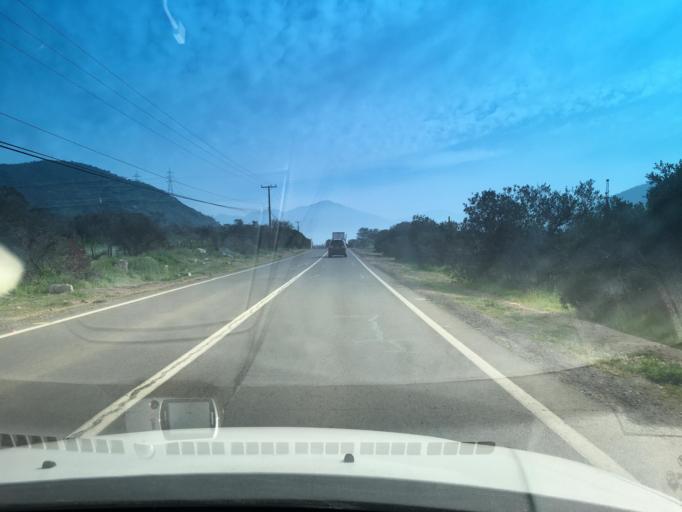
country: CL
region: Santiago Metropolitan
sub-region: Provincia de Chacabuco
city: Lampa
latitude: -33.1472
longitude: -70.9126
